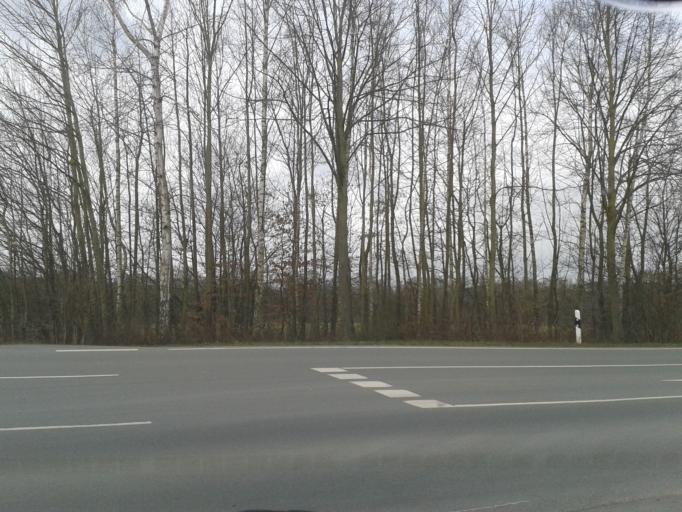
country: DE
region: North Rhine-Westphalia
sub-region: Regierungsbezirk Detmold
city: Blomberg
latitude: 51.9165
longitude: 9.1444
